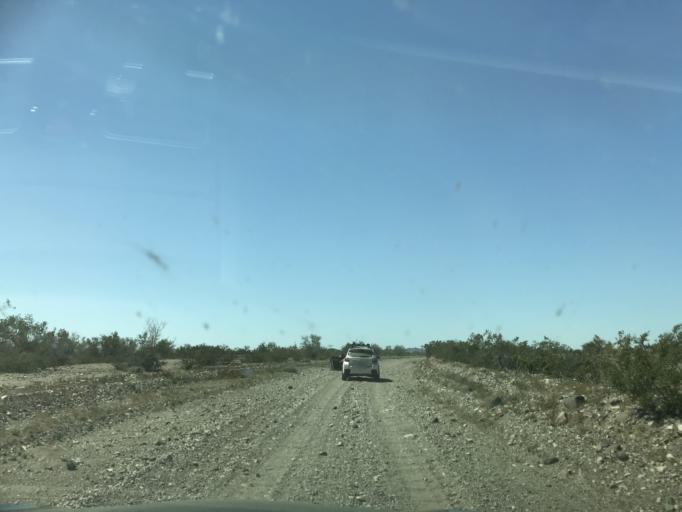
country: US
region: California
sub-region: Riverside County
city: Mesa Verde
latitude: 33.4740
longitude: -114.9471
